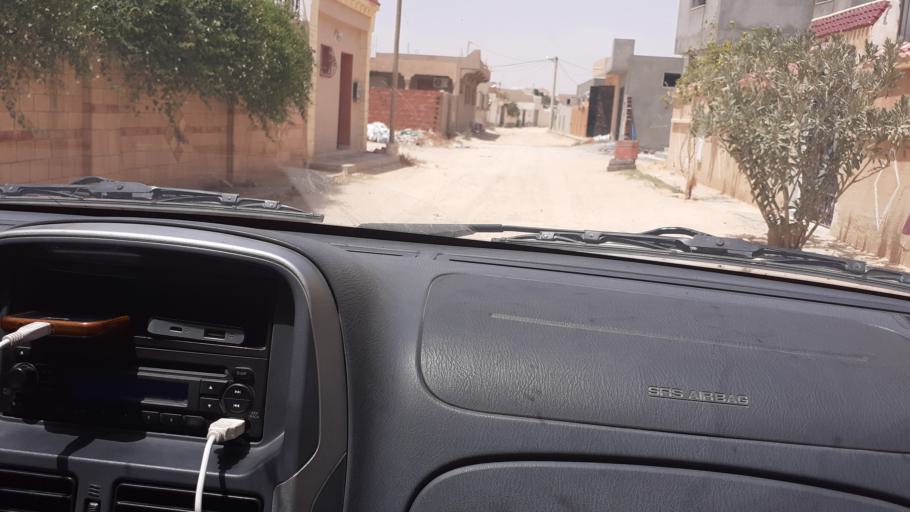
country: TN
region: Qabis
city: Matmata
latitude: 33.6117
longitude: 10.2903
